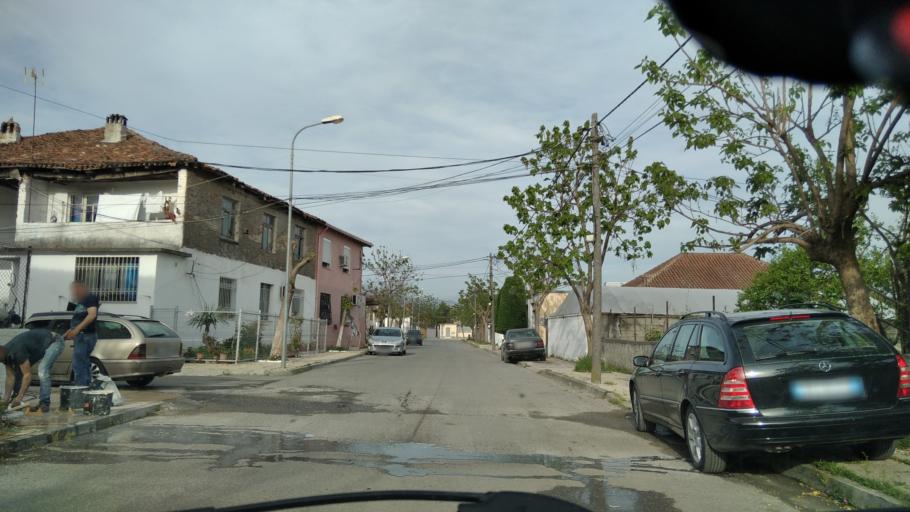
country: AL
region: Shkoder
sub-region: Rrethi i Shkodres
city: Shkoder
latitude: 42.0793
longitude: 19.5007
